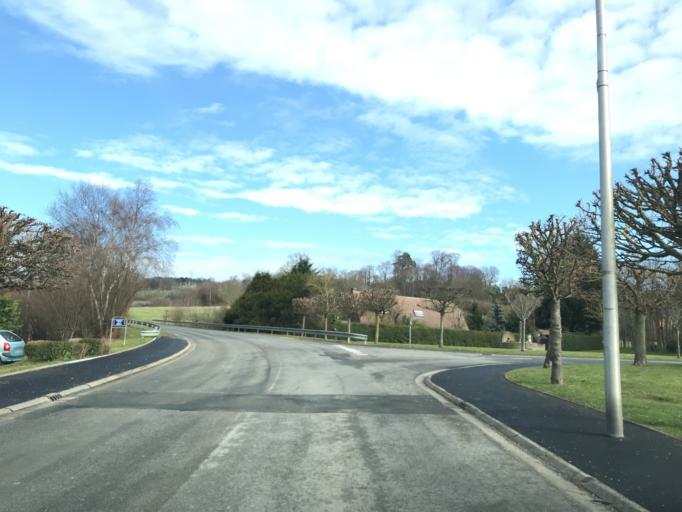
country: FR
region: Lower Normandy
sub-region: Departement du Calvados
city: Dives-sur-Mer
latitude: 49.2833
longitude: -0.0948
